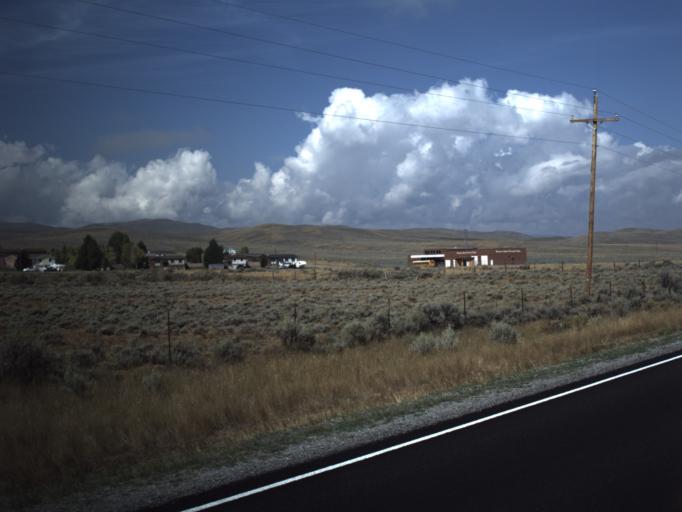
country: US
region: Utah
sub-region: Rich County
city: Randolph
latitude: 41.5852
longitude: -111.1681
